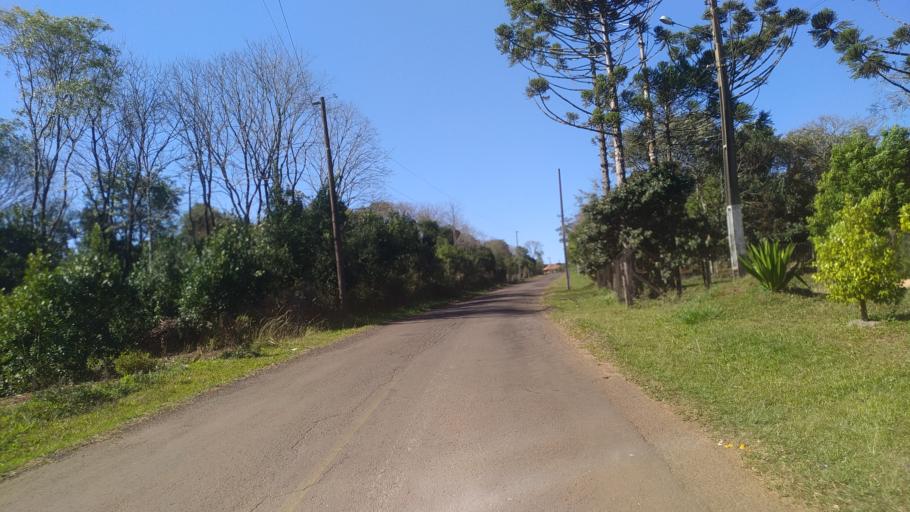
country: BR
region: Santa Catarina
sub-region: Chapeco
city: Chapeco
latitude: -27.1486
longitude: -52.6193
